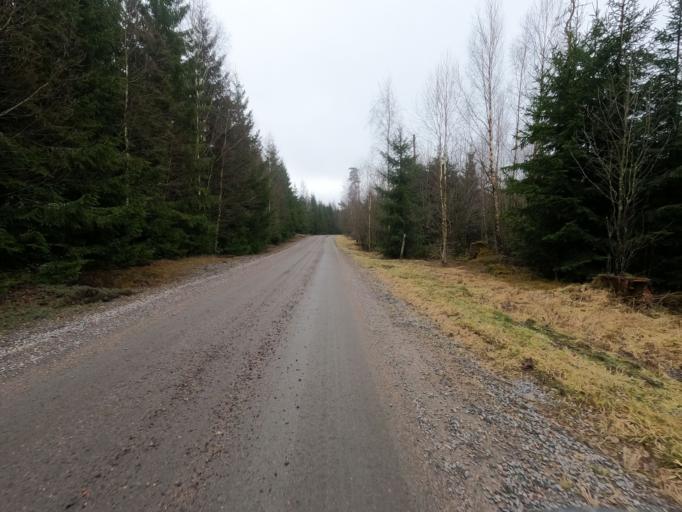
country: SE
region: Kronoberg
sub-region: Markaryds Kommun
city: Stromsnasbruk
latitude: 56.8169
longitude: 13.5671
